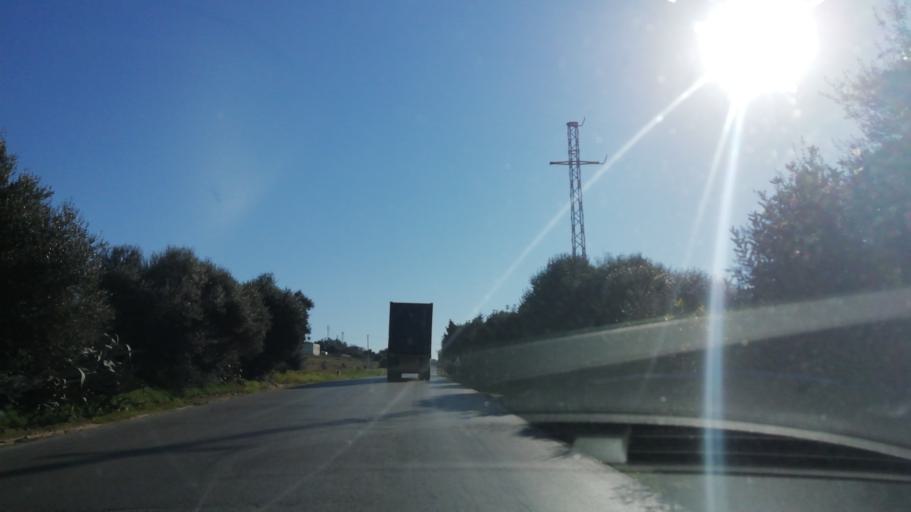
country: DZ
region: Relizane
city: Smala
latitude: 35.6805
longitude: 0.8002
